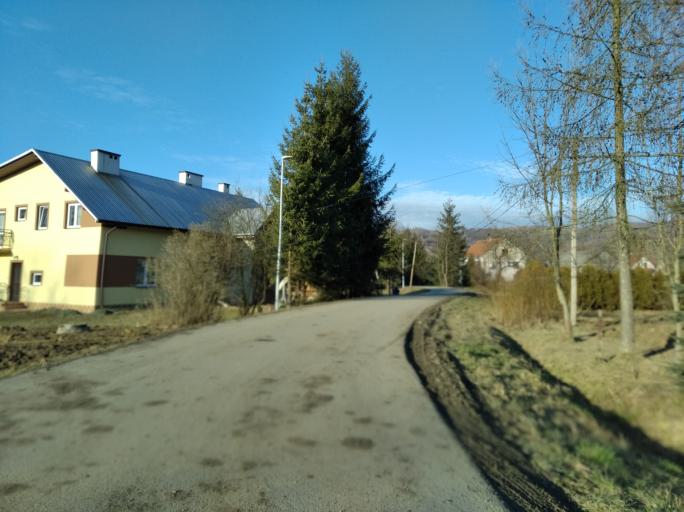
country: PL
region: Subcarpathian Voivodeship
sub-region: Powiat strzyzowski
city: Strzyzow
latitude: 49.8340
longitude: 21.8353
